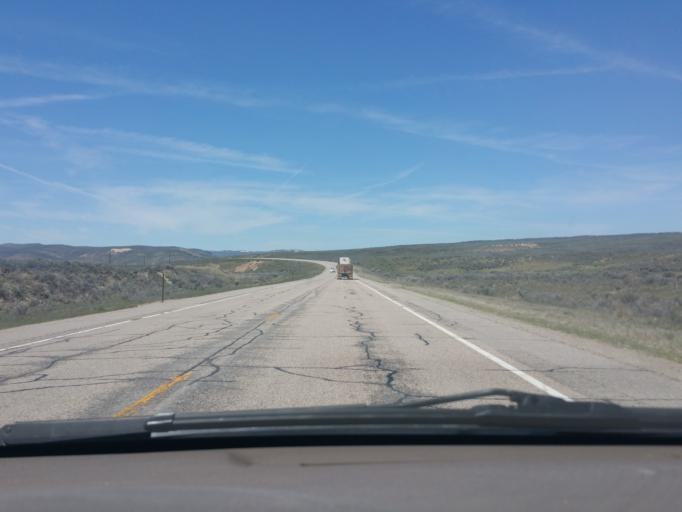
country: US
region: Wyoming
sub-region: Lincoln County
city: Kemmerer
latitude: 41.8157
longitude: -110.6572
